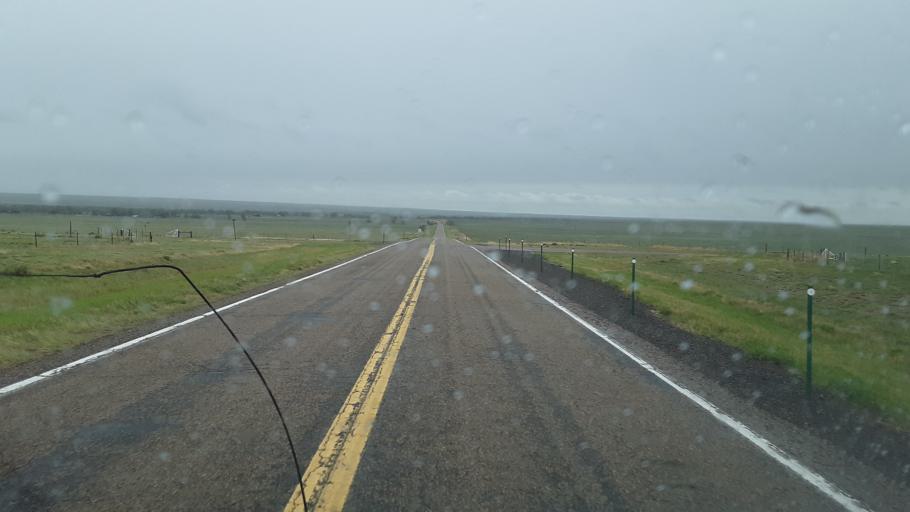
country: US
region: Colorado
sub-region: Lincoln County
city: Hugo
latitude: 38.8667
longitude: -103.1257
